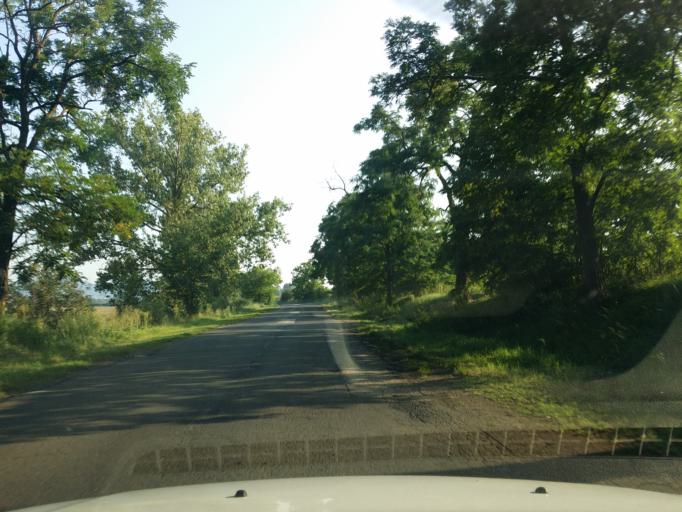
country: HU
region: Borsod-Abauj-Zemplen
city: Abaujszanto
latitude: 48.3272
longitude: 21.2020
